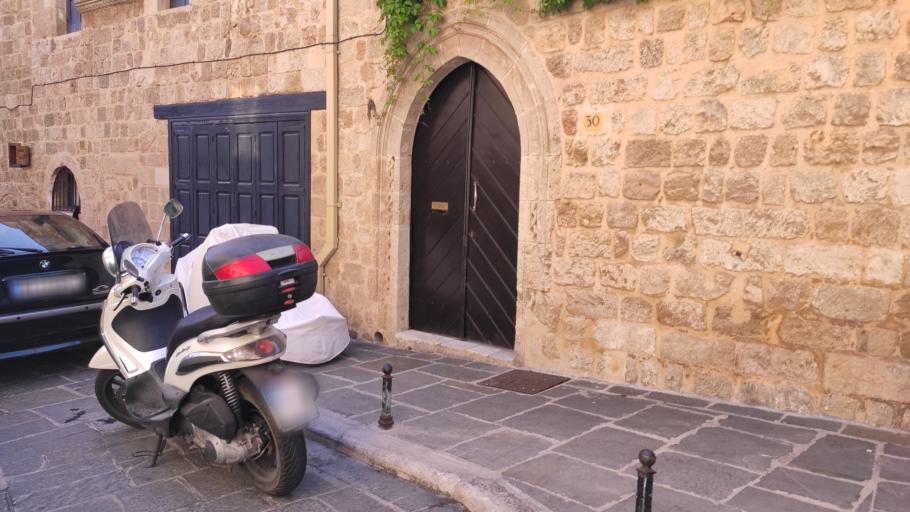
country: GR
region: South Aegean
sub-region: Nomos Dodekanisou
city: Rodos
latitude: 36.4402
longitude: 28.2286
